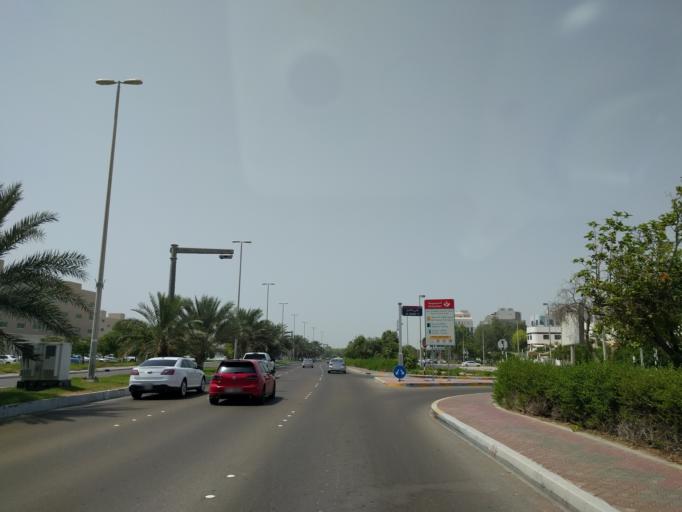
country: AE
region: Abu Dhabi
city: Abu Dhabi
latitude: 24.4305
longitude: 54.4297
